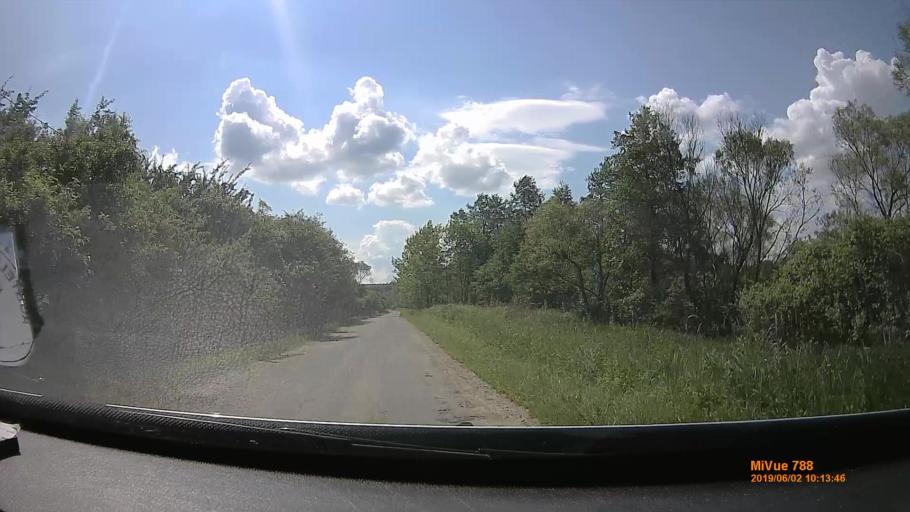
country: HU
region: Borsod-Abauj-Zemplen
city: Szendro
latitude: 48.5132
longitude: 20.7870
